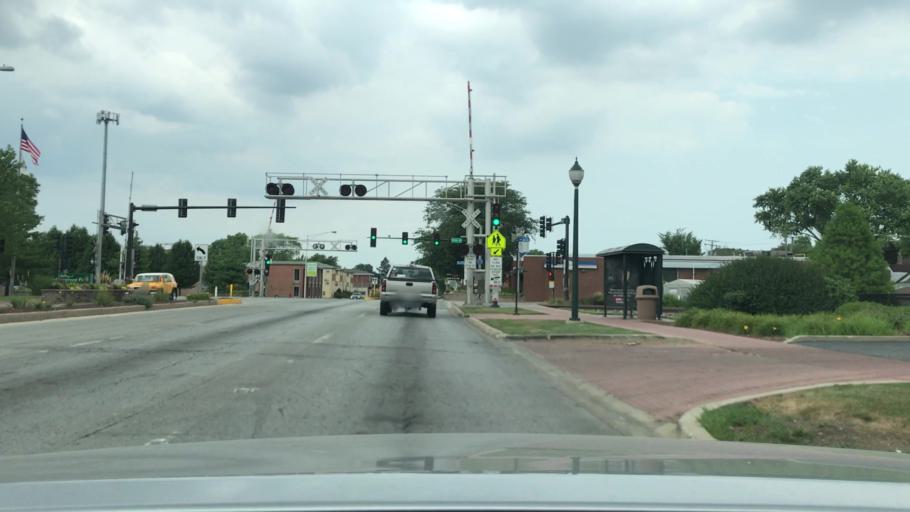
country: US
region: Illinois
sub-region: Cook County
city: Evergreen Park
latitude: 41.7218
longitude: -87.7017
